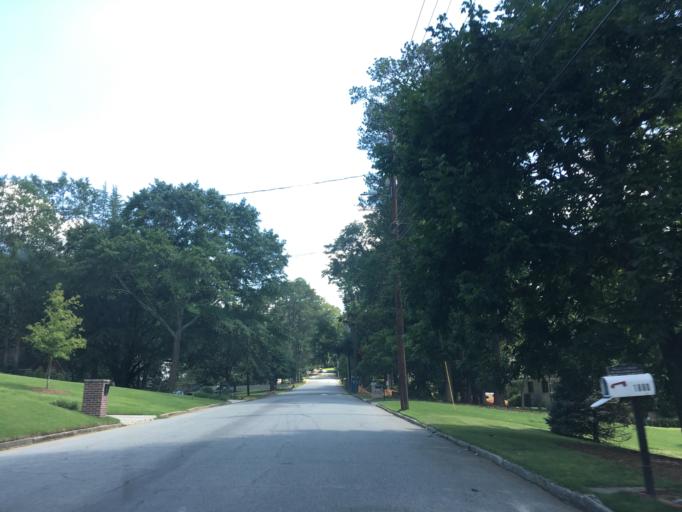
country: US
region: Georgia
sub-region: DeKalb County
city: Druid Hills
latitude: 33.8059
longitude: -84.3601
